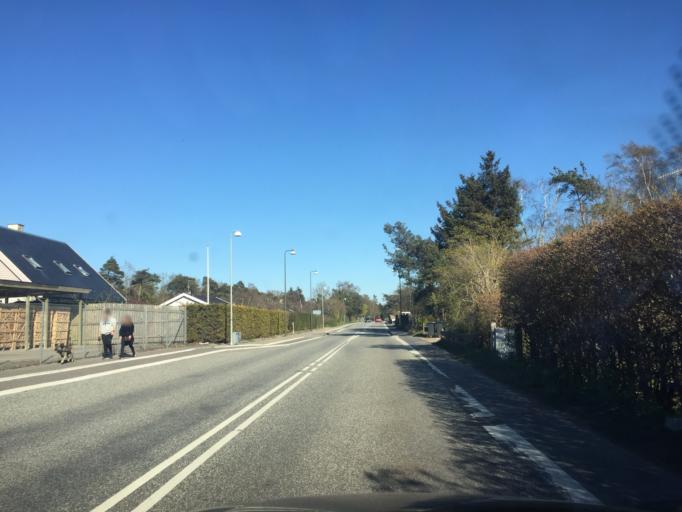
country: DK
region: Capital Region
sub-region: Halsnaes Kommune
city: Frederiksvaerk
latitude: 56.0060
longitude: 11.9940
